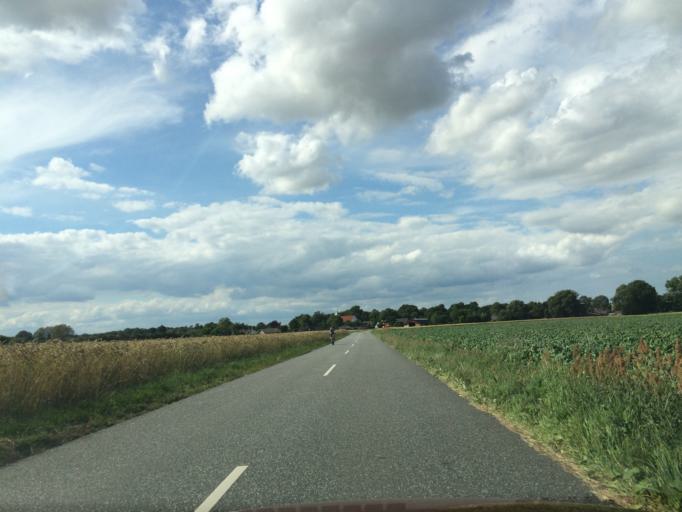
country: DK
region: Central Jutland
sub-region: Syddjurs Kommune
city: Ebeltoft
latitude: 56.2986
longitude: 10.6989
